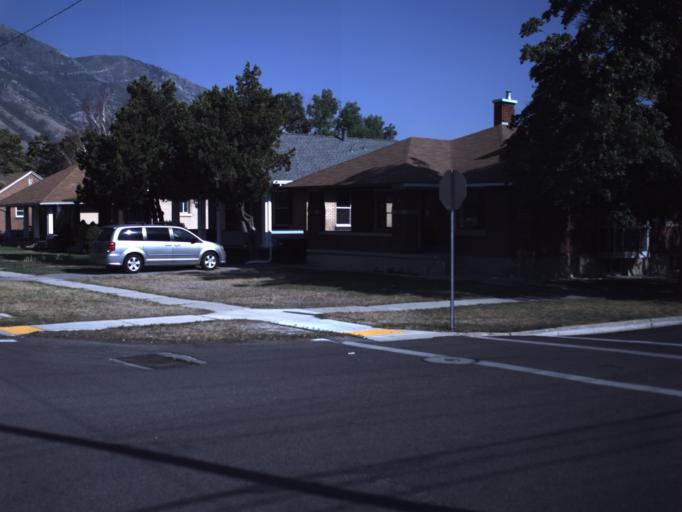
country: US
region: Utah
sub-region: Utah County
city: Provo
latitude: 40.2337
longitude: -111.6728
